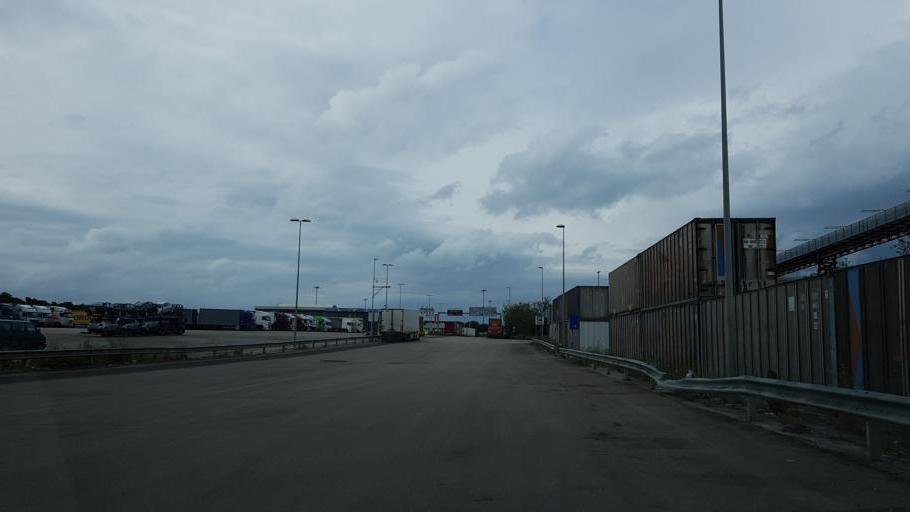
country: IT
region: Apulia
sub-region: Provincia di Brindisi
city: Materdomini
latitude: 40.6410
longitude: 17.9630
